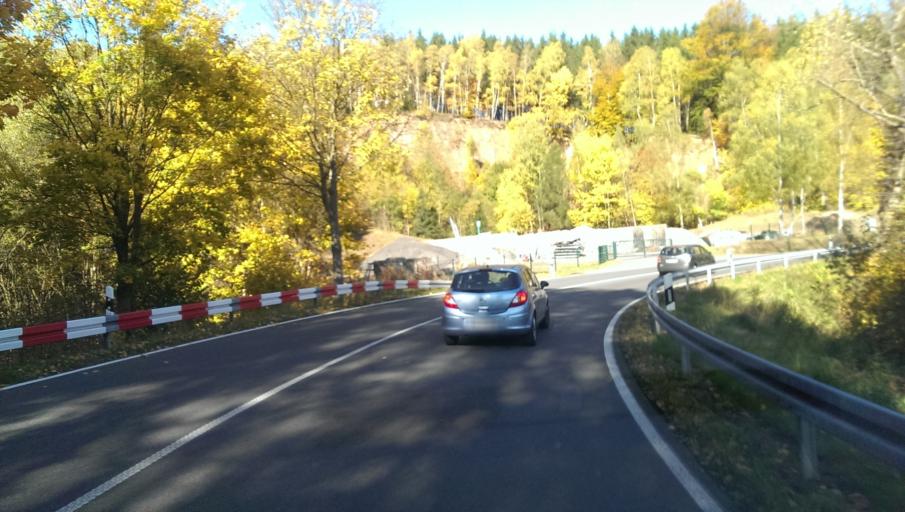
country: DE
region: Saxony
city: Geising
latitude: 50.7592
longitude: 13.7780
